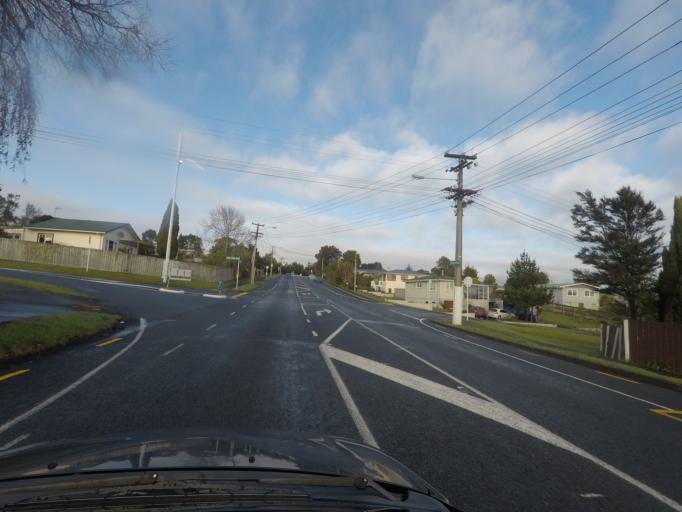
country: NZ
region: Auckland
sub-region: Auckland
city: Waitakere
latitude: -36.8992
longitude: 174.6166
